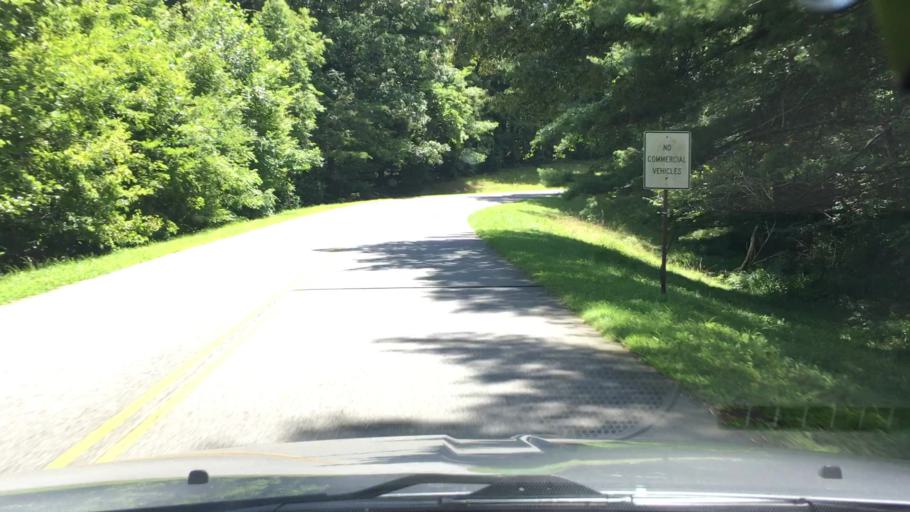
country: US
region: North Carolina
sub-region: Buncombe County
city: Biltmore Forest
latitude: 35.5860
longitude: -82.4778
